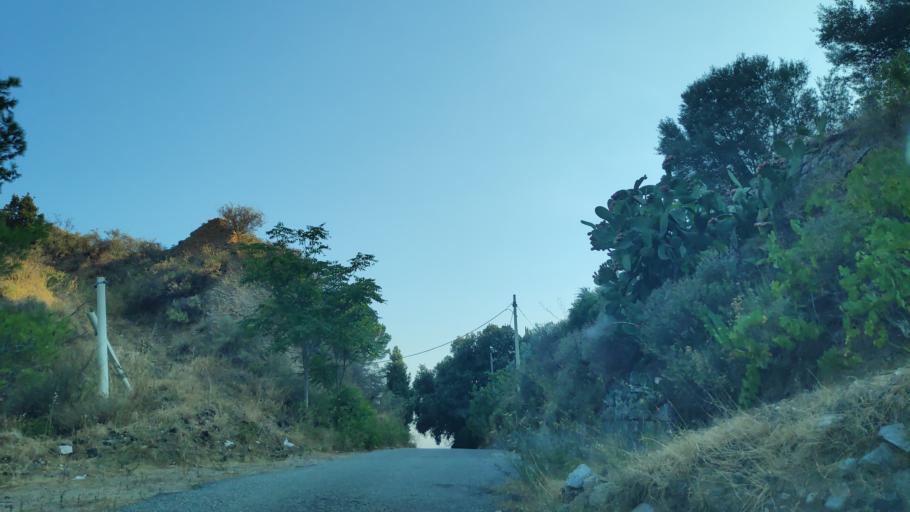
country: IT
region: Calabria
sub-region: Provincia di Reggio Calabria
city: Placanica
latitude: 38.4108
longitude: 16.4298
